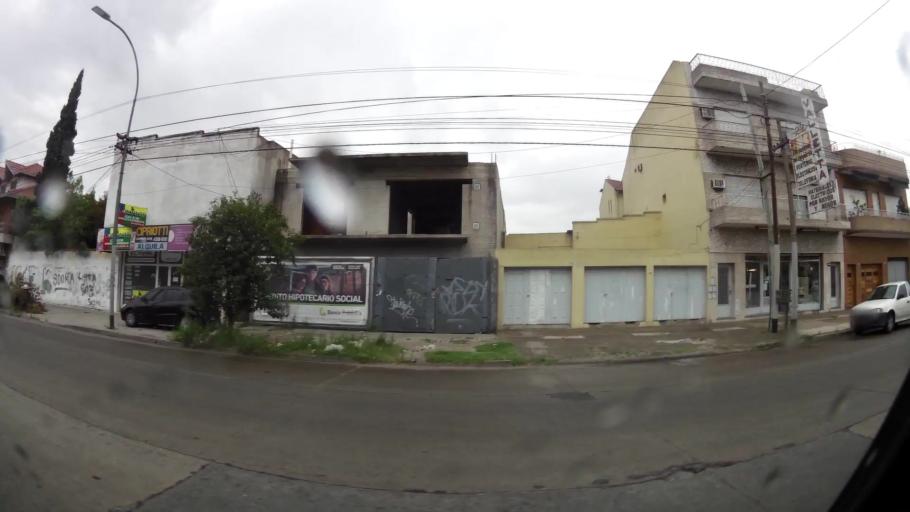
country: AR
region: Buenos Aires
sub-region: Partido de Lanus
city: Lanus
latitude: -34.6921
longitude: -58.4044
